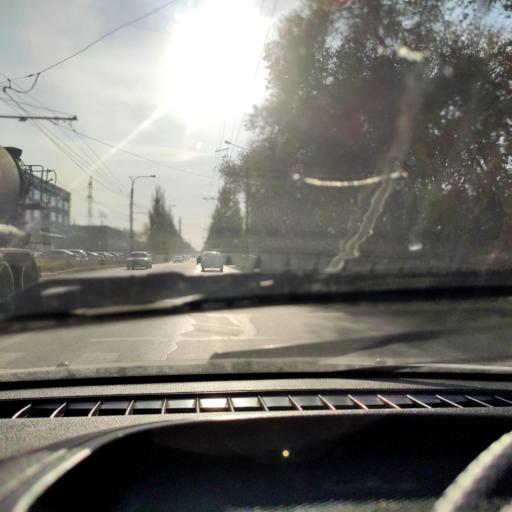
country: RU
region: Samara
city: Tol'yatti
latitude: 53.5670
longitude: 49.4574
